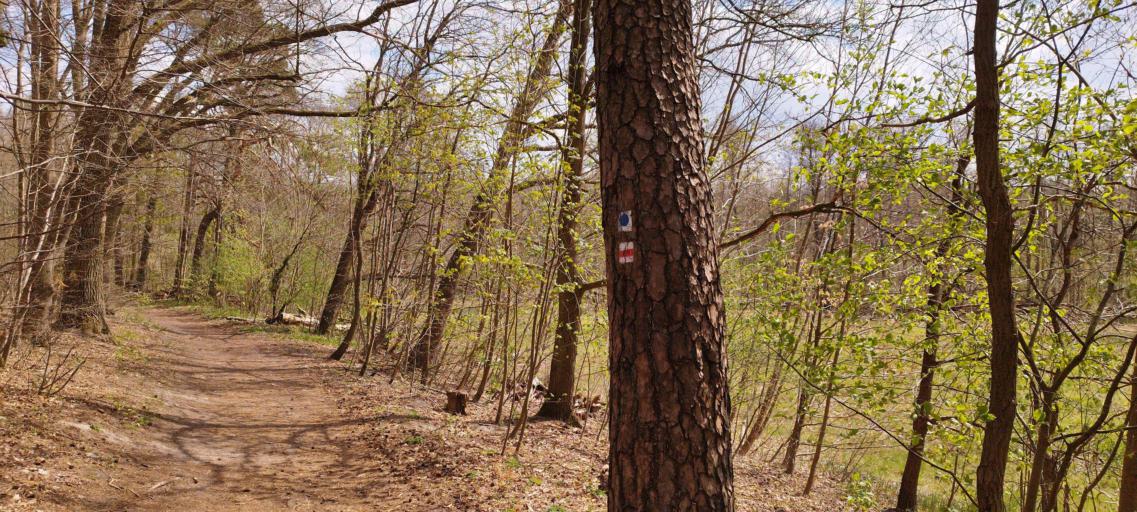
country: DE
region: Brandenburg
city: Erkner
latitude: 52.4188
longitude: 13.7695
